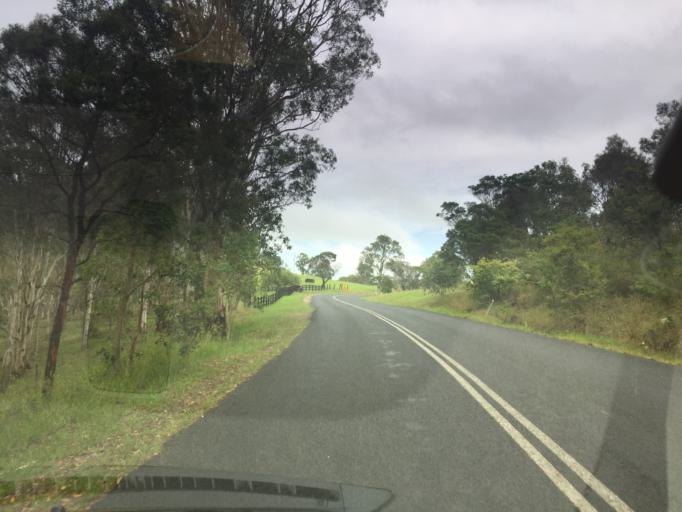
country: AU
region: New South Wales
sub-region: Bega Valley
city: Bega
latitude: -36.7580
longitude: 149.6849
